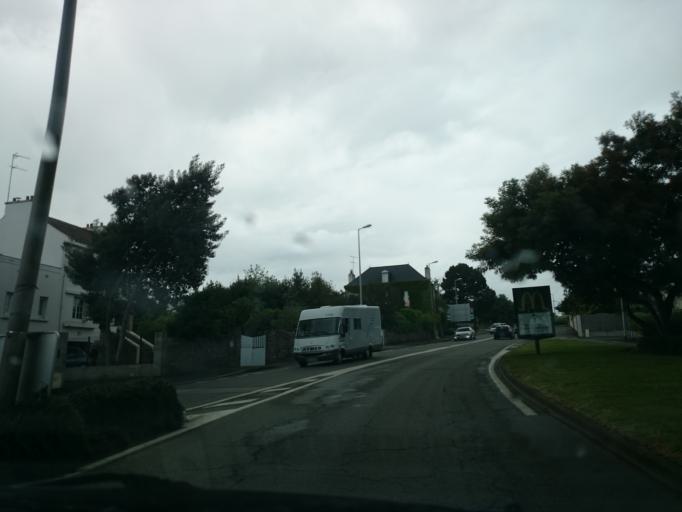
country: FR
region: Brittany
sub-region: Departement du Morbihan
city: Vannes
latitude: 47.6390
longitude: -2.7682
